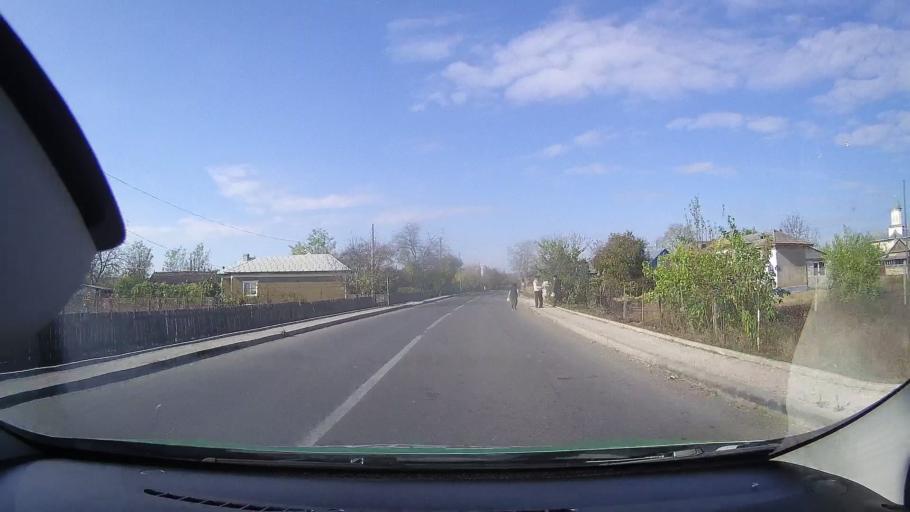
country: RO
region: Tulcea
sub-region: Comuna Valea Nucarilor
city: Iazurile
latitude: 45.0221
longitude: 28.9488
